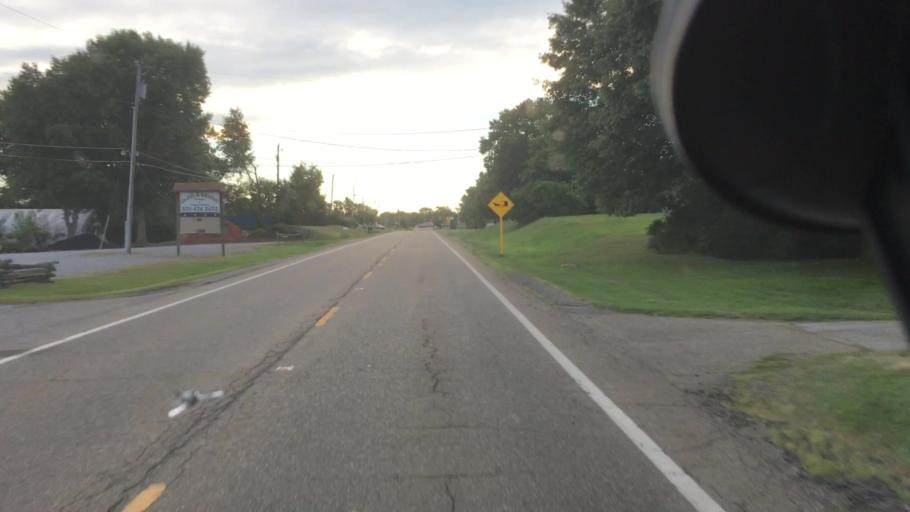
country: US
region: Ohio
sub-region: Columbiana County
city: East Palestine
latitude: 40.8581
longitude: -80.5420
